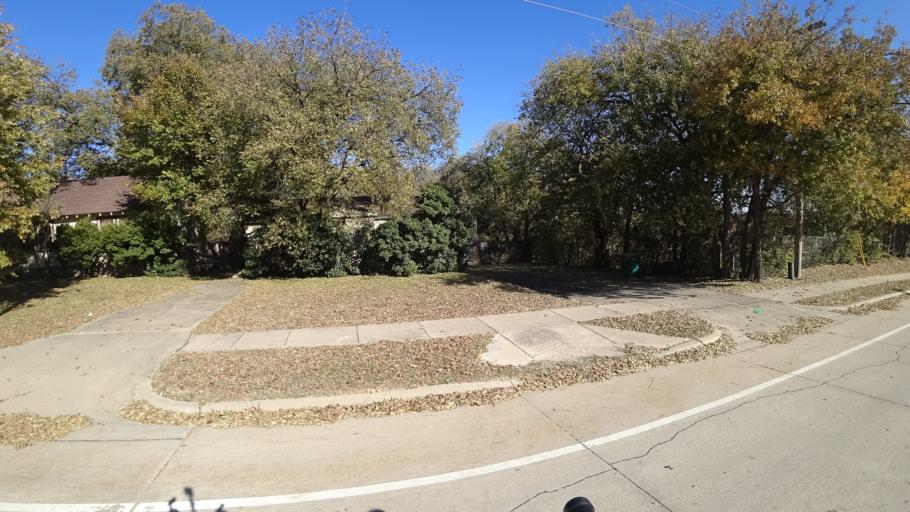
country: US
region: Texas
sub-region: Denton County
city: Lewisville
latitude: 33.0492
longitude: -96.9894
